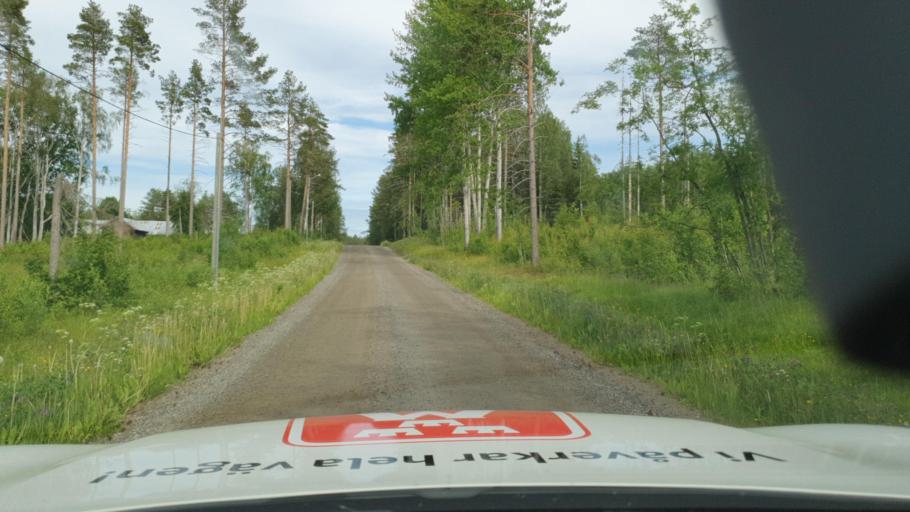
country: SE
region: Vaesterbotten
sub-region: Robertsfors Kommun
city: Robertsfors
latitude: 64.3730
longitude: 21.0530
